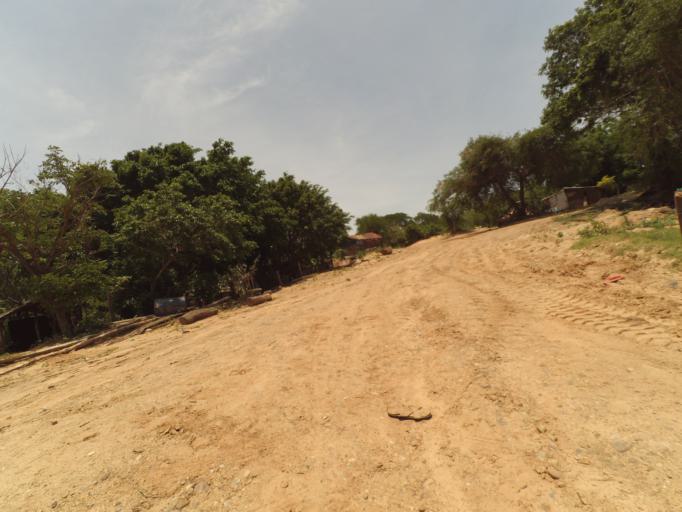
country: BO
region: Santa Cruz
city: Santa Cruz de la Sierra
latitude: -17.8173
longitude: -63.2576
